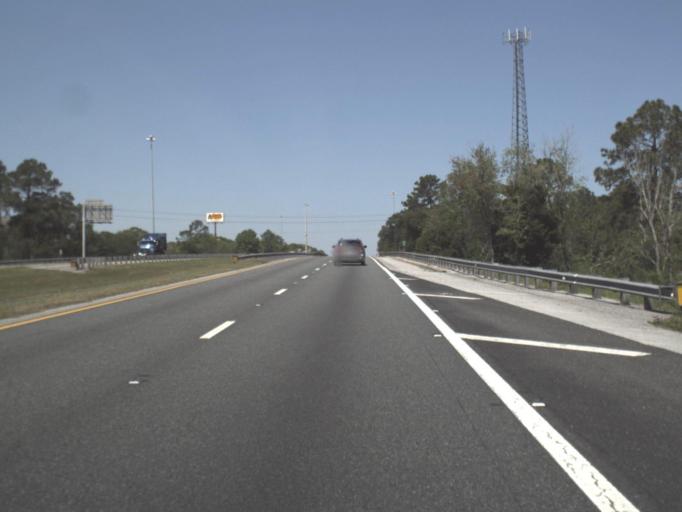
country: US
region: Florida
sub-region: Escambia County
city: Ensley
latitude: 30.5205
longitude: -87.3115
